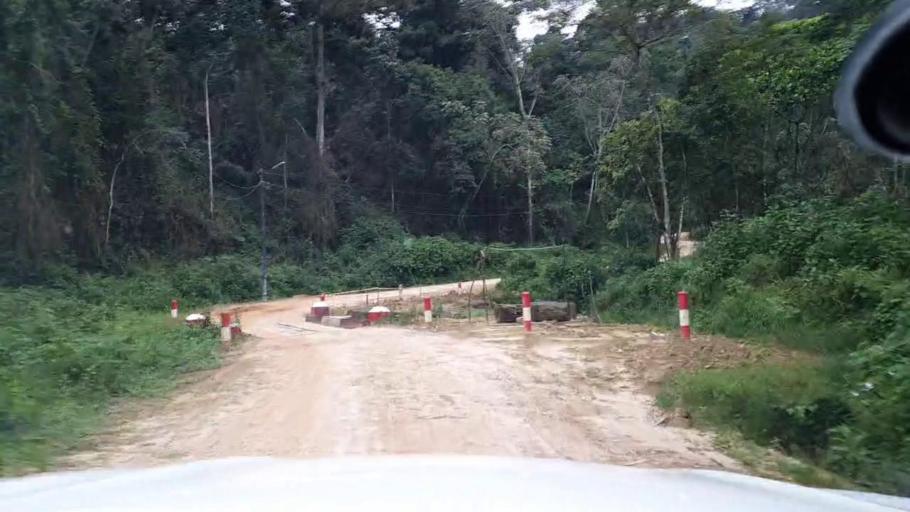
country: RW
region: Western Province
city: Cyangugu
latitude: -2.5695
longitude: 29.2252
